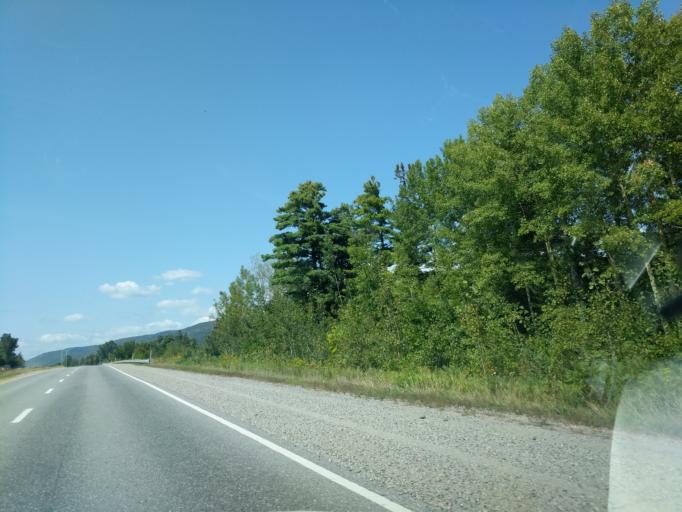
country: CA
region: Quebec
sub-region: Outaouais
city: Wakefield
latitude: 45.5128
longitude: -75.9790
